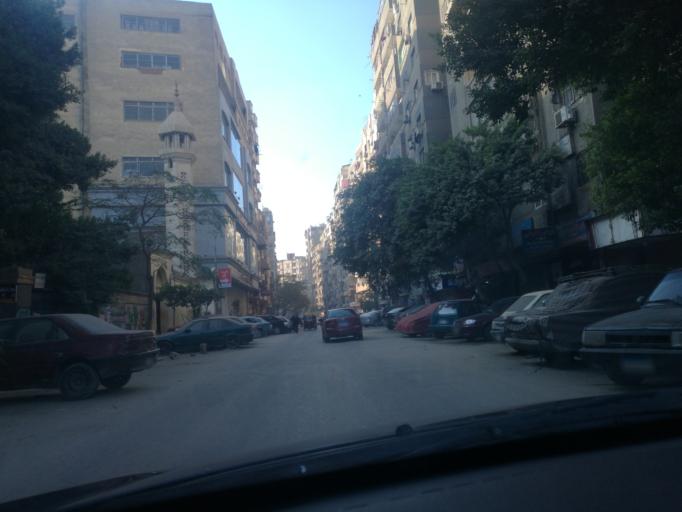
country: EG
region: Muhafazat al Qahirah
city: Cairo
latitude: 30.1055
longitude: 31.3071
